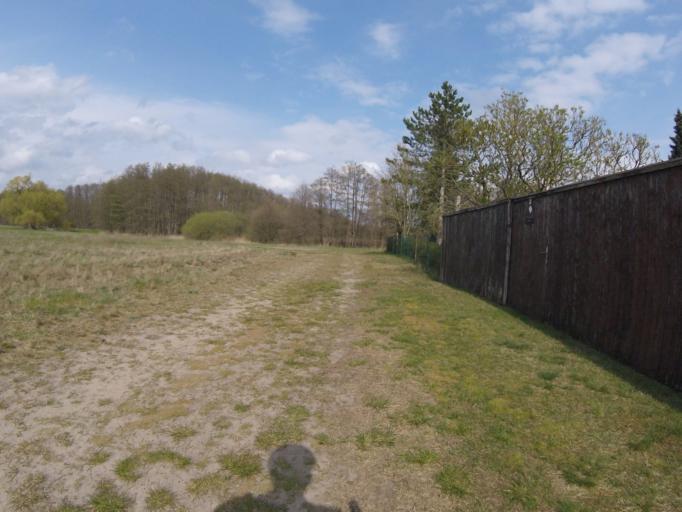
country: DE
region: Brandenburg
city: Bestensee
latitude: 52.2359
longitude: 13.6193
